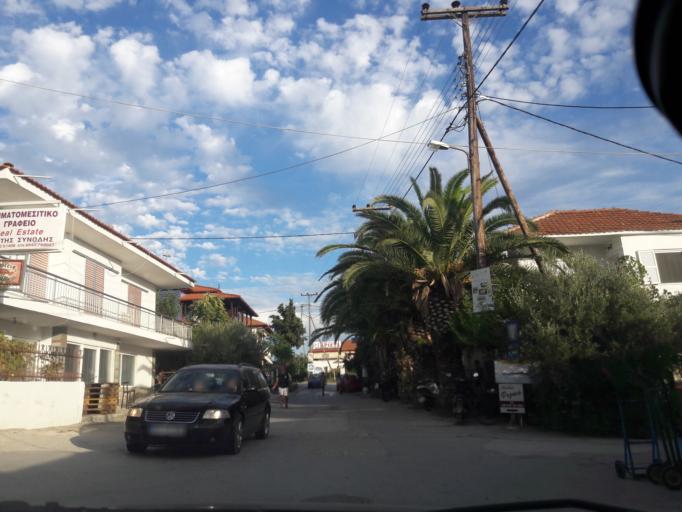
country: GR
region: Central Macedonia
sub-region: Nomos Chalkidikis
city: Nea Roda
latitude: 40.3316
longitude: 23.9205
